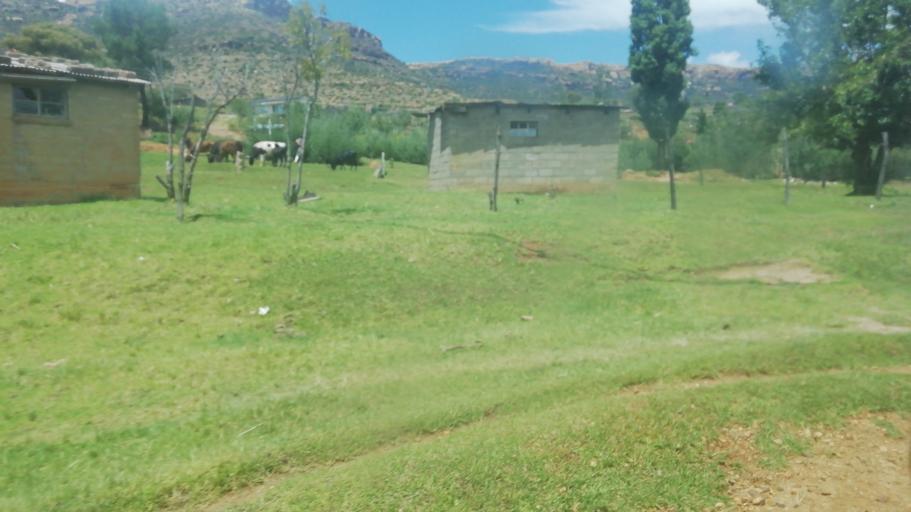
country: LS
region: Maseru
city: Nako
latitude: -29.6214
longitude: 27.5170
